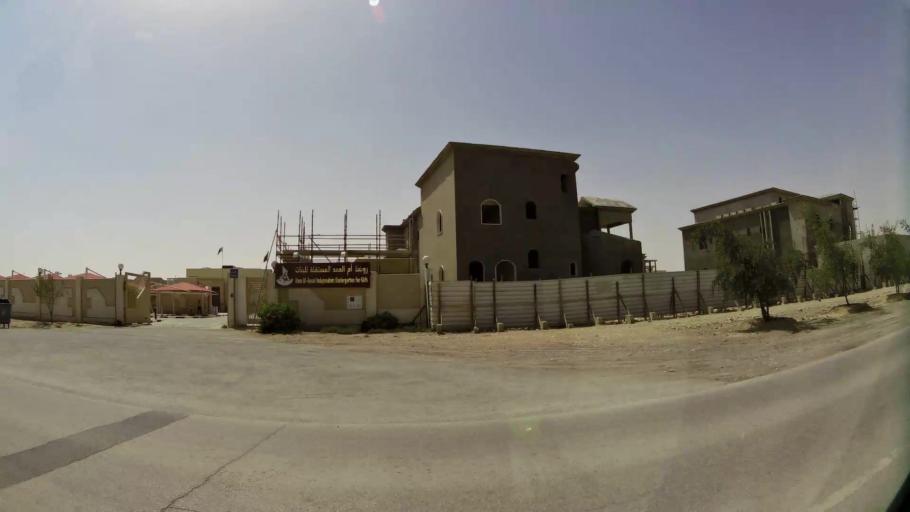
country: QA
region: Baladiyat Umm Salal
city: Umm Salal Muhammad
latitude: 25.3737
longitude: 51.4212
